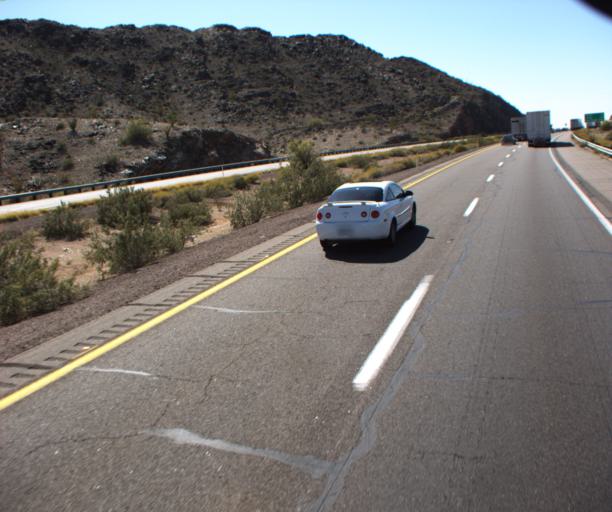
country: US
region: Arizona
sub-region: Yuma County
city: Wellton
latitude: 32.7261
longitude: -113.7438
